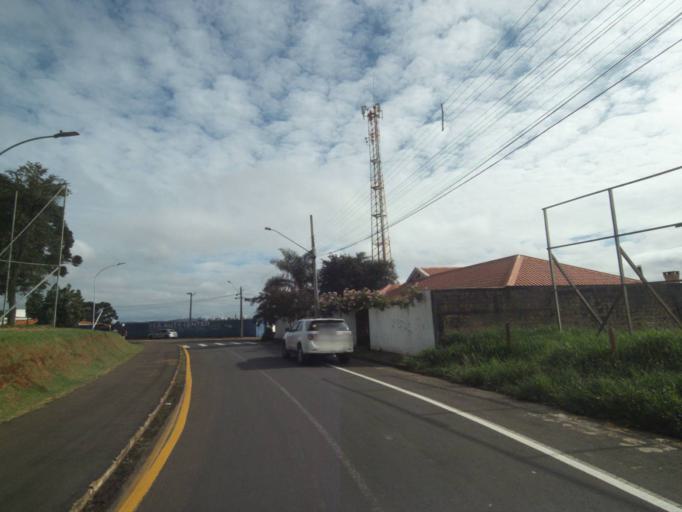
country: BR
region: Parana
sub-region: Telemaco Borba
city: Telemaco Borba
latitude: -24.3328
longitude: -50.6081
